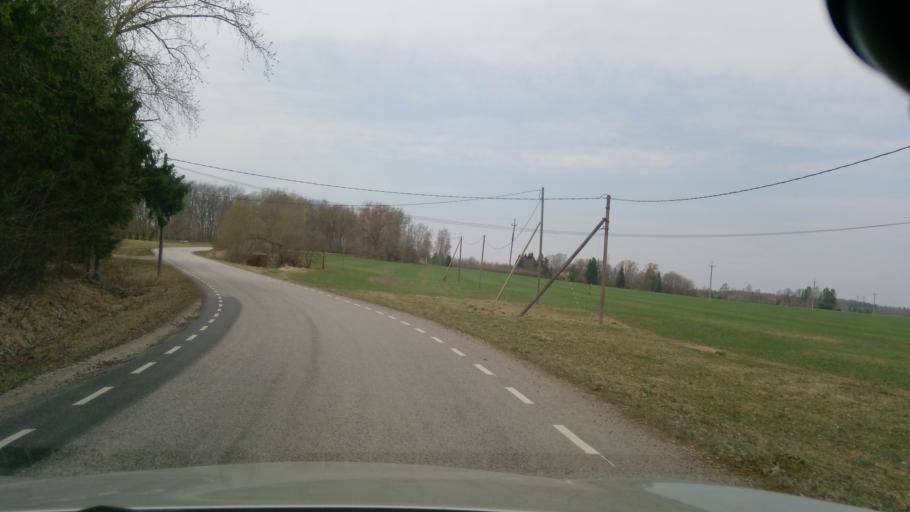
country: EE
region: Jaervamaa
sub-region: Tueri vald
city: Sarevere
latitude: 58.7832
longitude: 25.4781
